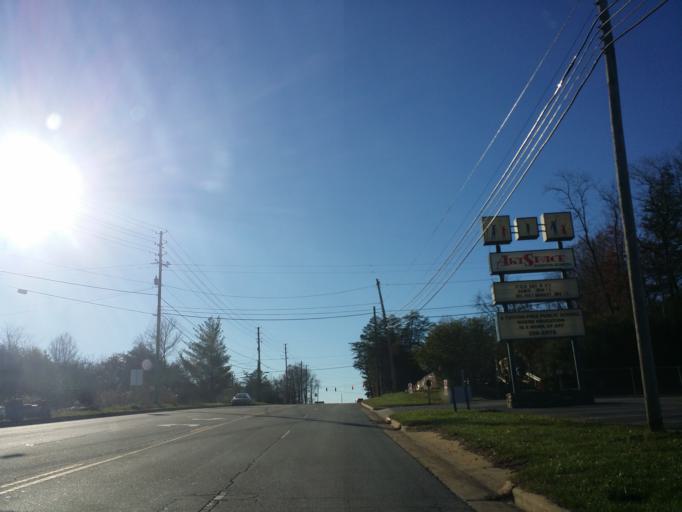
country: US
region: North Carolina
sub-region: Buncombe County
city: Swannanoa
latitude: 35.5941
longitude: -82.4284
